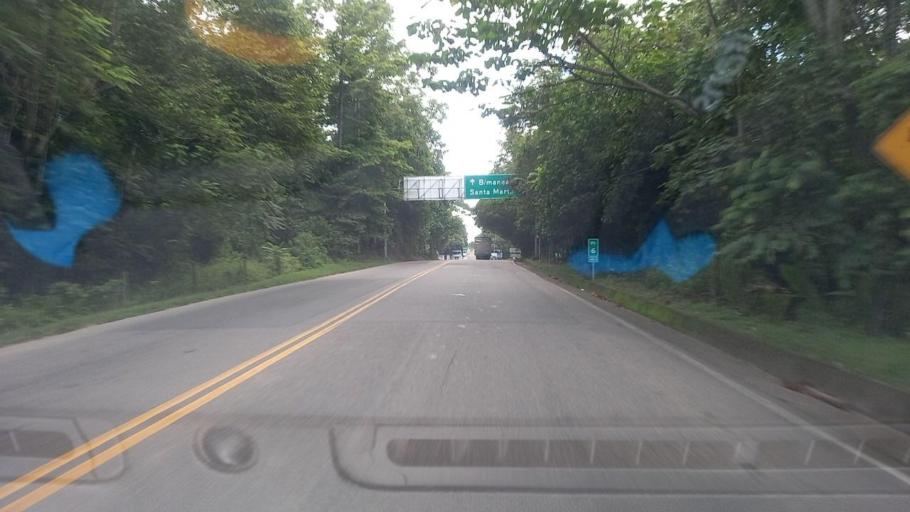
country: CO
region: Santander
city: Sabana de Torres
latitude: 7.1297
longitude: -73.5659
